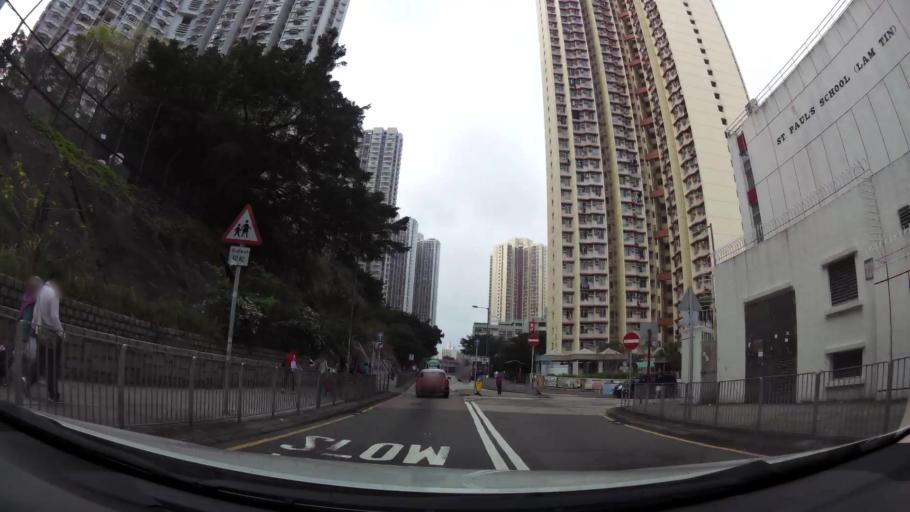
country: HK
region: Kowloon City
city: Kowloon
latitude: 22.3089
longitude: 114.2378
